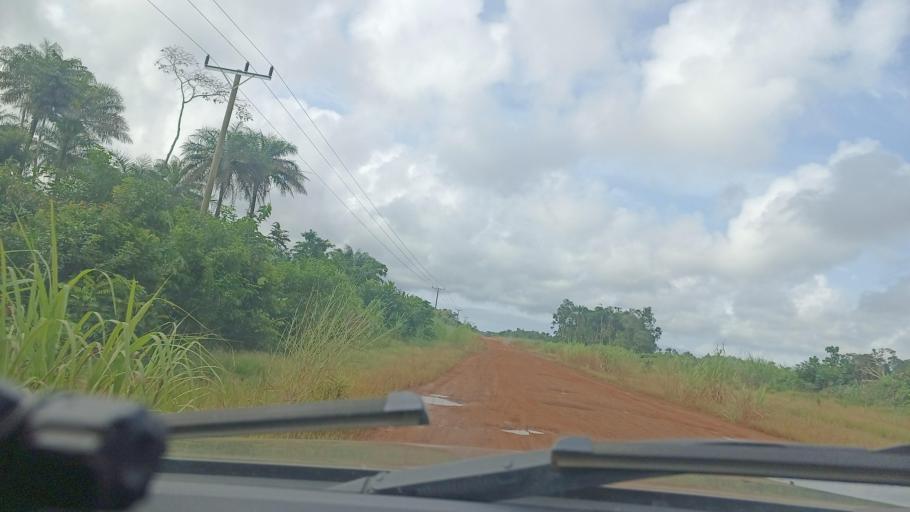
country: LR
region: Grand Cape Mount
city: Robertsport
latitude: 6.6775
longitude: -11.1378
